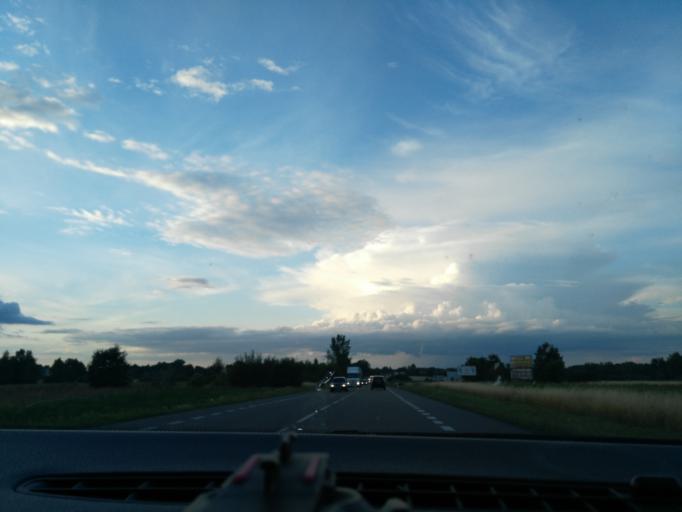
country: PL
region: Lublin Voivodeship
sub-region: Powiat lubartowski
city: Serniki
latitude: 51.4127
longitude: 22.6401
